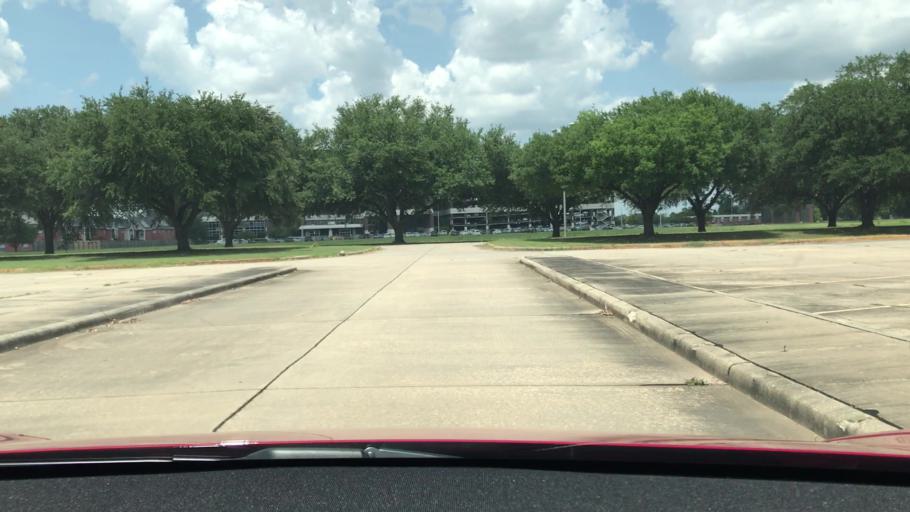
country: US
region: Louisiana
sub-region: Bossier Parish
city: Bossier City
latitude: 32.4290
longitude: -93.7069
